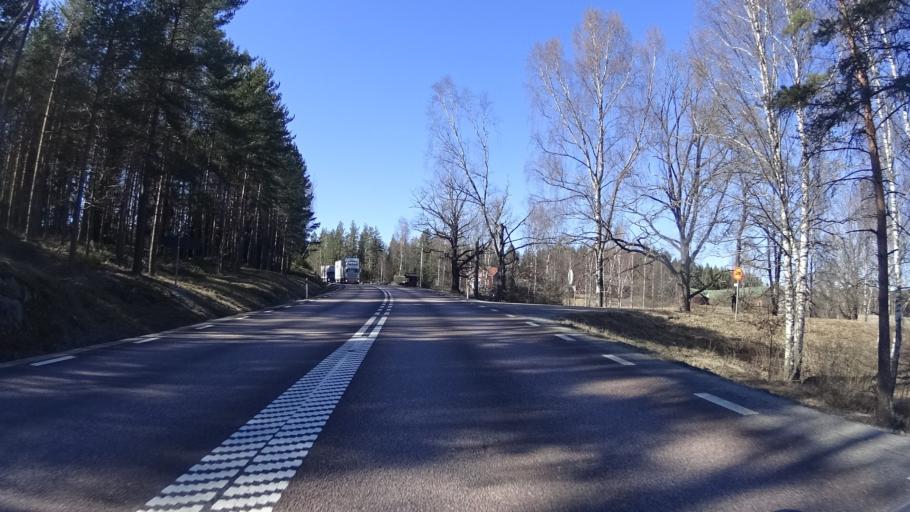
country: SE
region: Vaermland
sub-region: Sunne Kommun
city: Sunne
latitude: 59.6559
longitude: 12.9432
